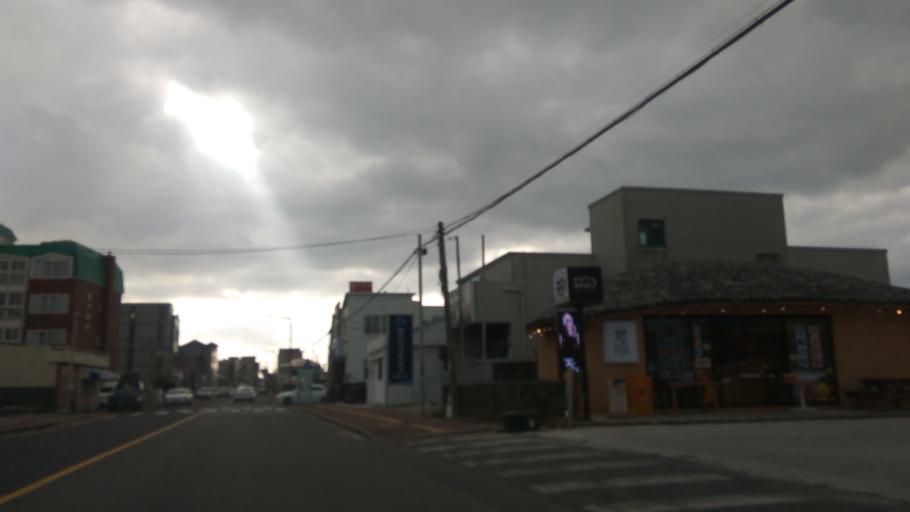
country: KR
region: Jeju-do
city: Jeju-si
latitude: 33.4622
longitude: 126.9325
